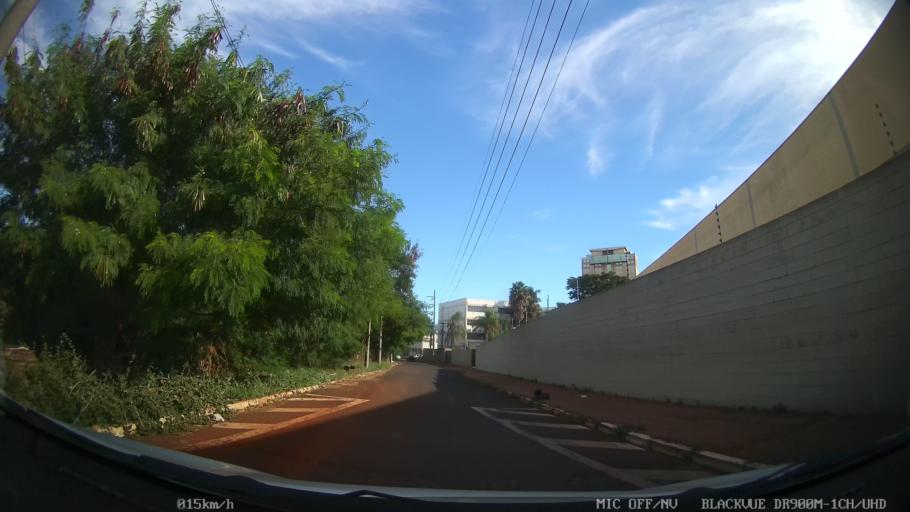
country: BR
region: Sao Paulo
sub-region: Araraquara
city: Araraquara
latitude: -21.8041
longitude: -48.1714
